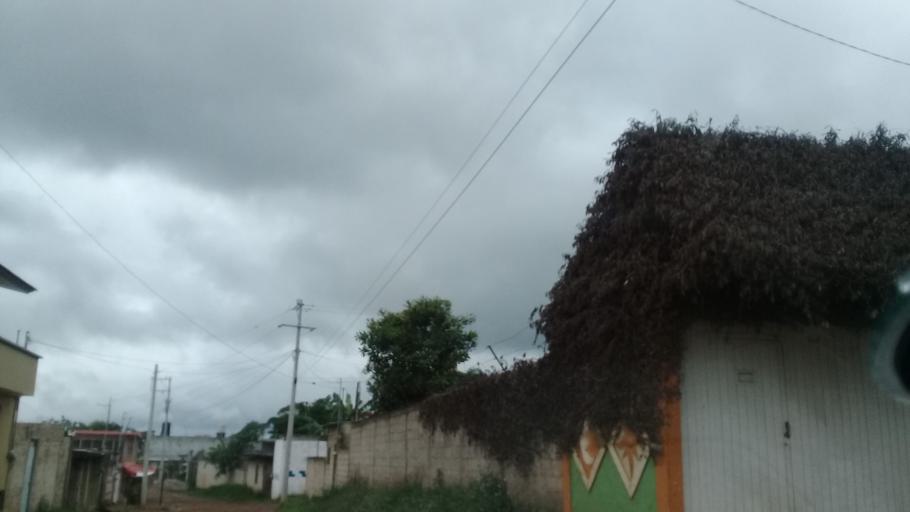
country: MX
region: Veracruz
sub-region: Emiliano Zapata
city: Las Trancas
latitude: 19.4966
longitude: -96.8626
